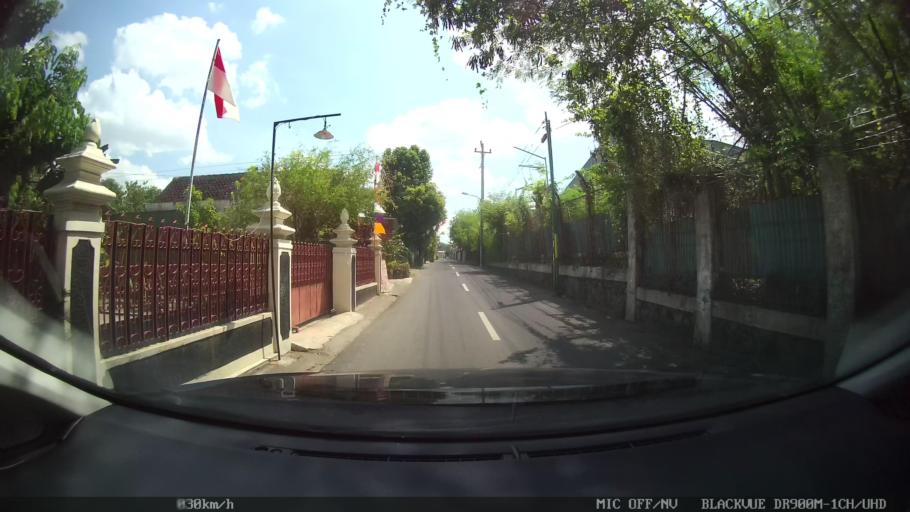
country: ID
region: Daerah Istimewa Yogyakarta
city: Yogyakarta
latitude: -7.8275
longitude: 110.3880
